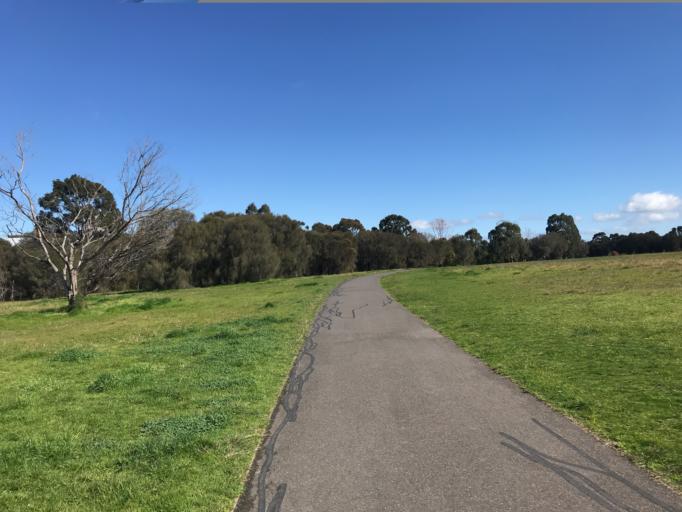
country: AU
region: Victoria
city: Parkville
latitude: -37.7926
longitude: 144.9533
